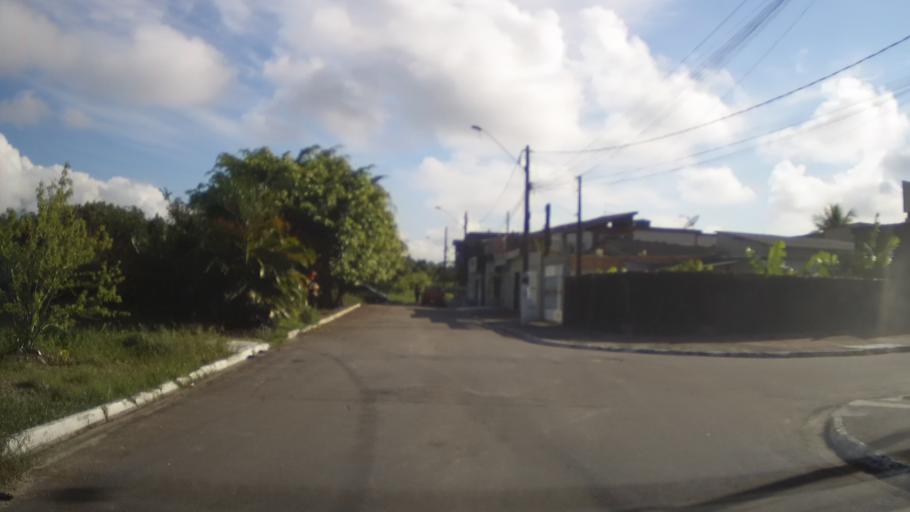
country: BR
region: Sao Paulo
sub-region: Praia Grande
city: Praia Grande
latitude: -24.0119
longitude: -46.4809
